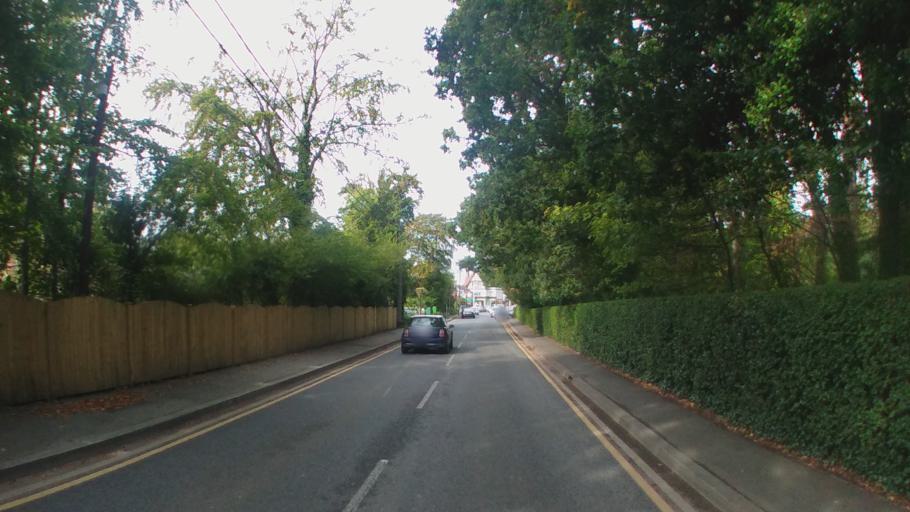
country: IE
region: Leinster
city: Foxrock
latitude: 53.2660
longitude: -6.1835
